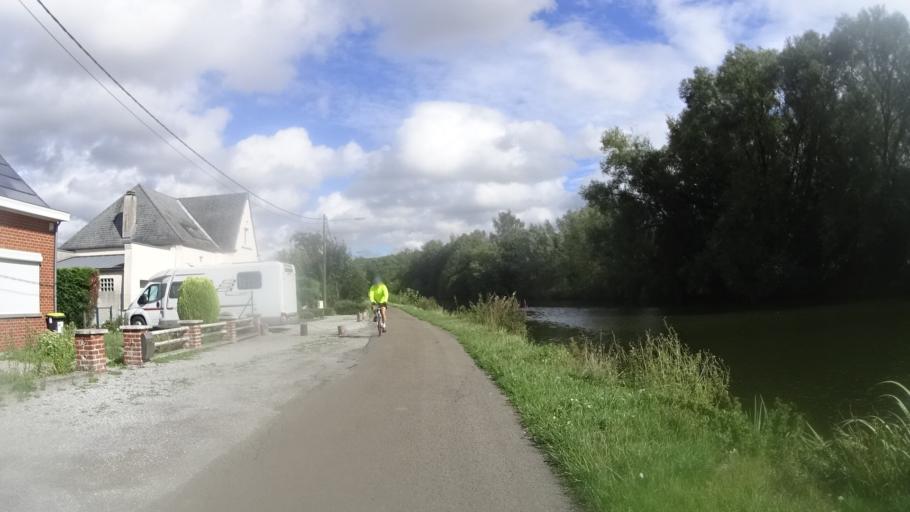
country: BE
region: Wallonia
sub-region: Province du Hainaut
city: Merbes-le-Chateau
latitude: 50.3142
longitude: 4.1861
